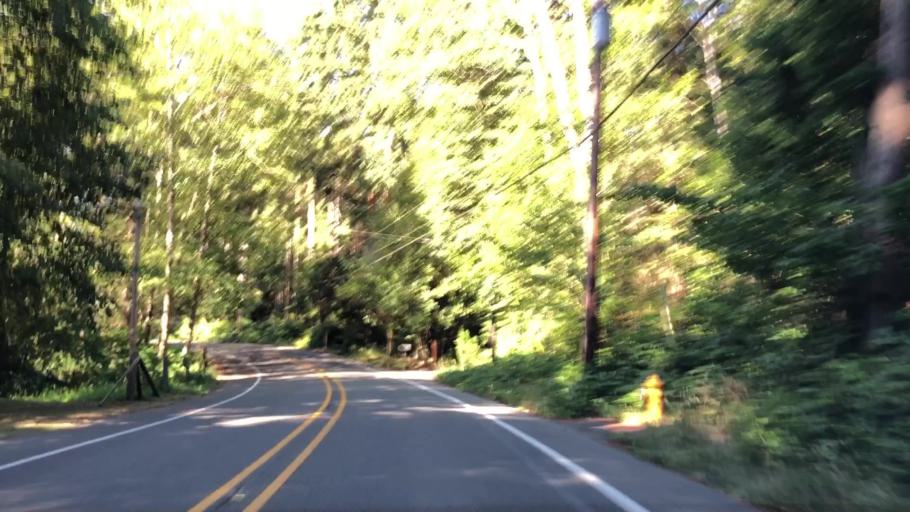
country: US
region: Washington
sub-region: Kitsap County
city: Kingston
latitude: 47.7767
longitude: -122.5012
